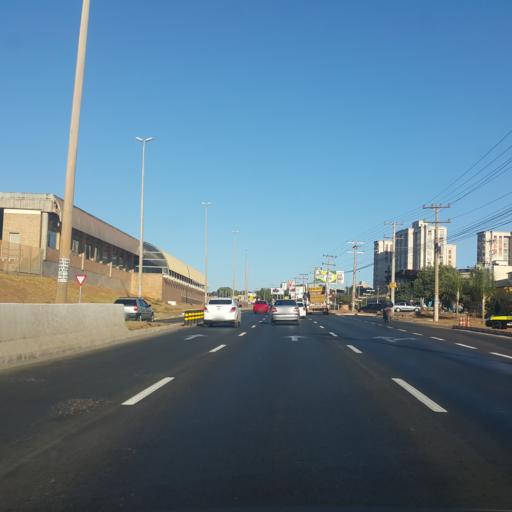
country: BR
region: Federal District
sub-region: Brasilia
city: Brasilia
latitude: -15.8350
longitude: -48.0852
